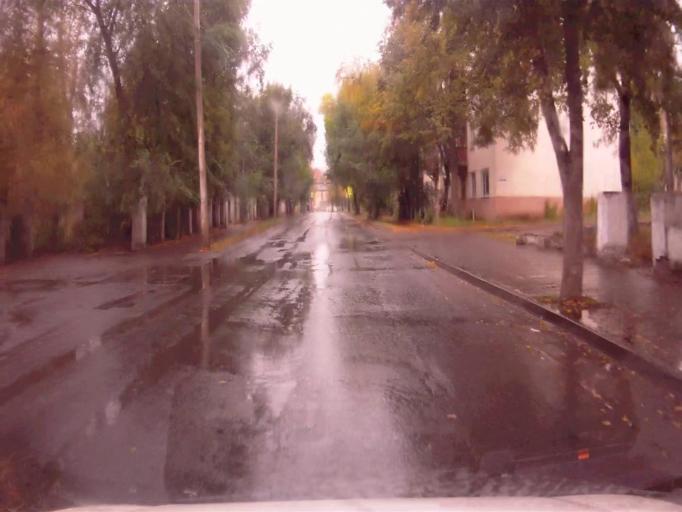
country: RU
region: Chelyabinsk
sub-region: Gorod Chelyabinsk
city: Chelyabinsk
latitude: 55.1924
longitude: 61.4119
